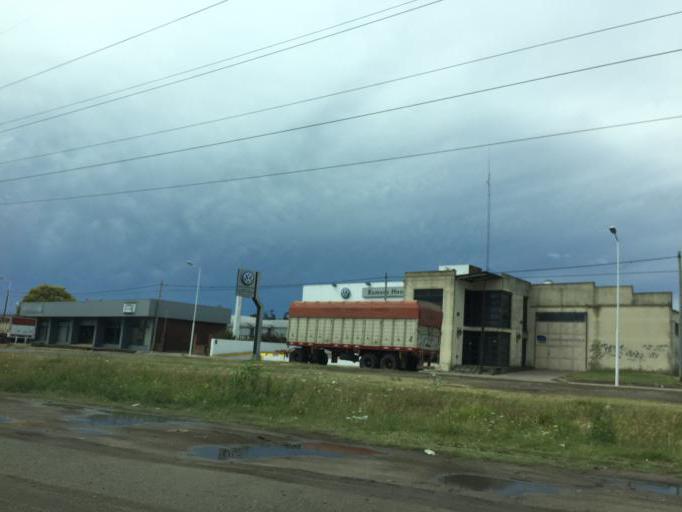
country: AR
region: Buenos Aires
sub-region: Partido de Tandil
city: Tandil
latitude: -37.3108
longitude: -59.1150
